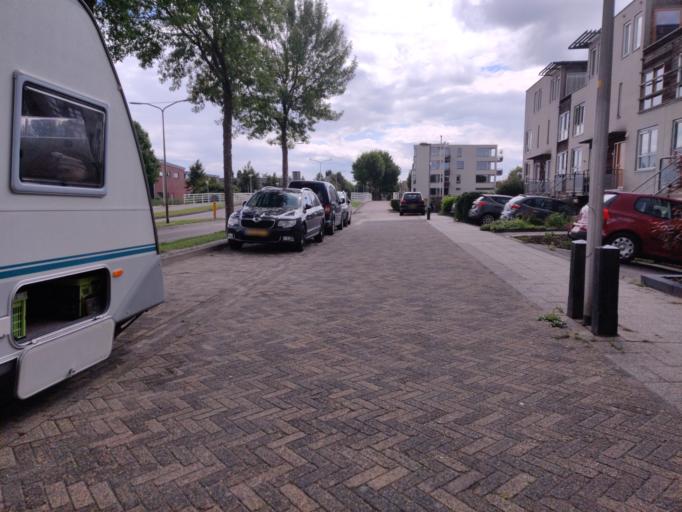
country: NL
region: Flevoland
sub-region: Gemeente Zeewolde
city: Zeewolde
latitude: 52.3345
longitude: 5.5180
